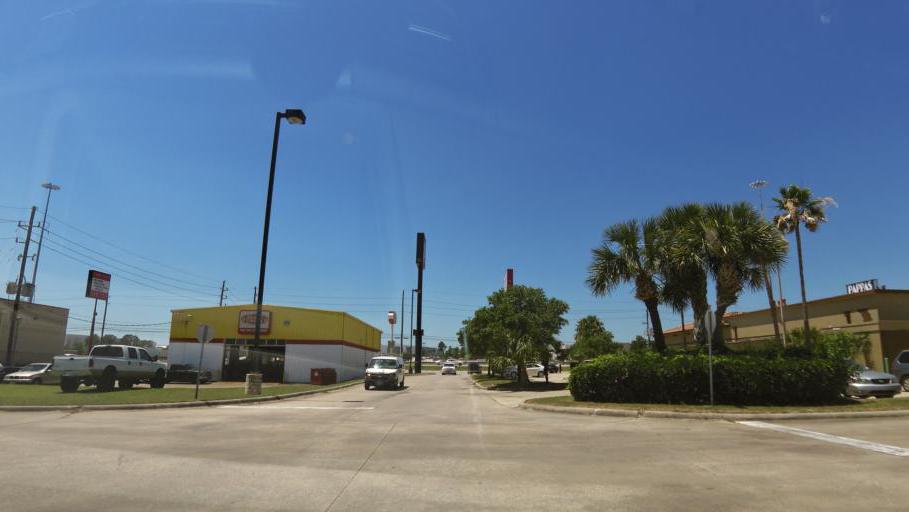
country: US
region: Texas
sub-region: Harris County
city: Humble
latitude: 30.0099
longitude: -95.2642
